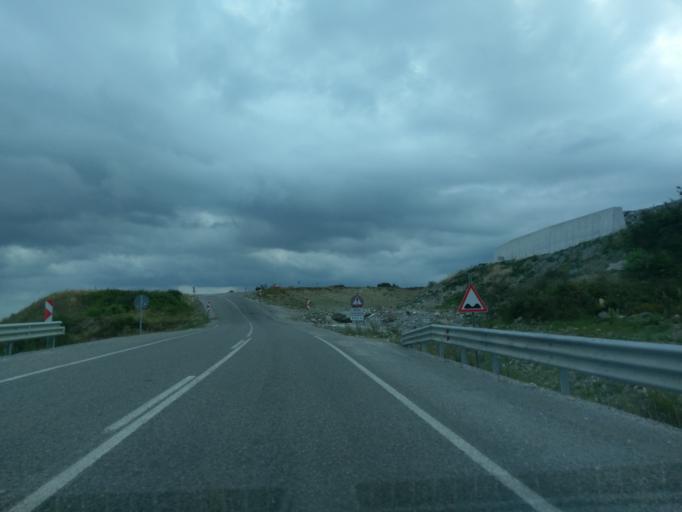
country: TR
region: Sinop
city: Helaldi
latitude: 41.9511
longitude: 34.3754
